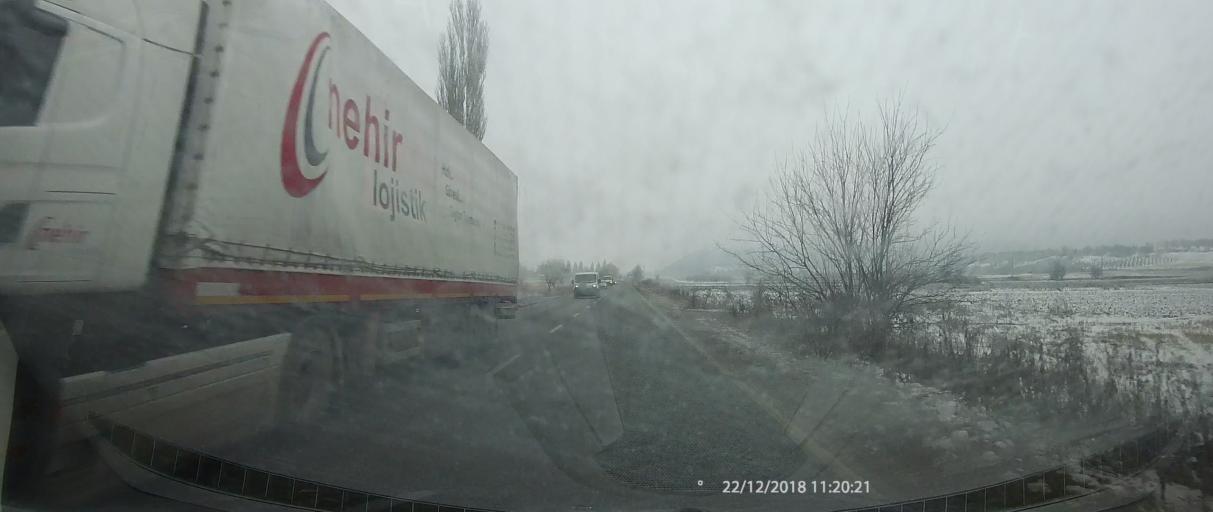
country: BG
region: Kyustendil
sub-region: Obshtina Kyustendil
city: Kyustendil
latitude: 42.2651
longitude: 22.8145
